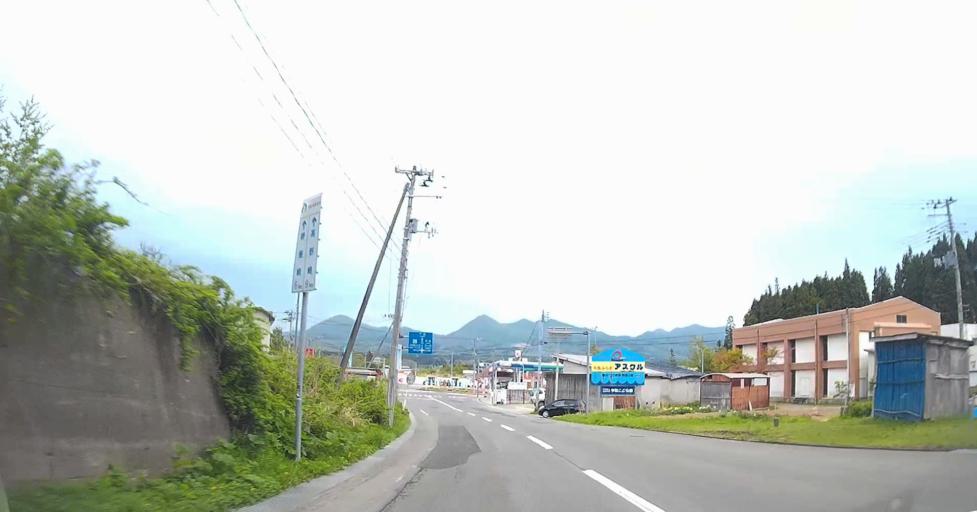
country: JP
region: Aomori
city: Goshogawara
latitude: 41.1764
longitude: 140.4900
